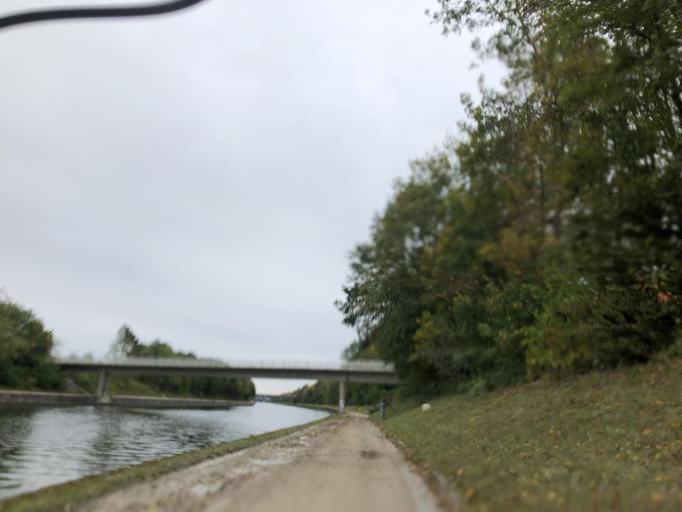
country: DE
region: Bavaria
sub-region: Regierungsbezirk Mittelfranken
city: Zirndorf
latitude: 49.4721
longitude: 10.9471
